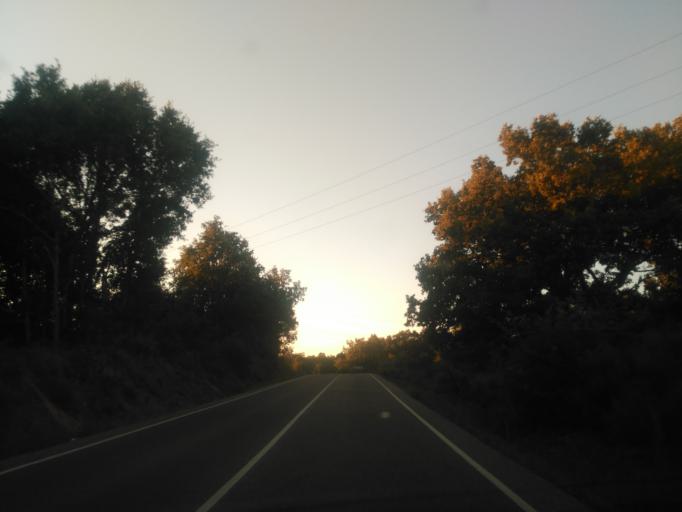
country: ES
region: Castille and Leon
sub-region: Provincia de Zamora
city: Puebla de Sanabria
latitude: 42.0765
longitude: -6.6212
